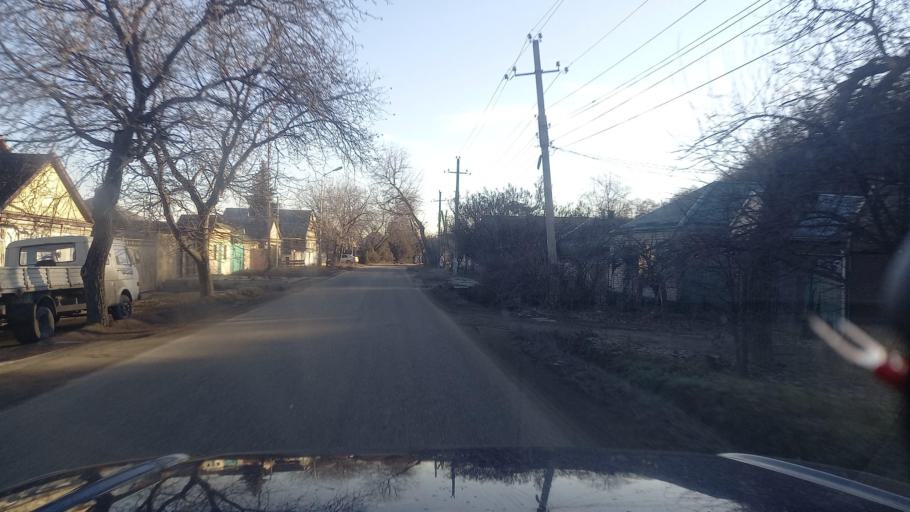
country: RU
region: Stavropol'skiy
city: Svobody
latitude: 44.0237
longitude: 43.0605
